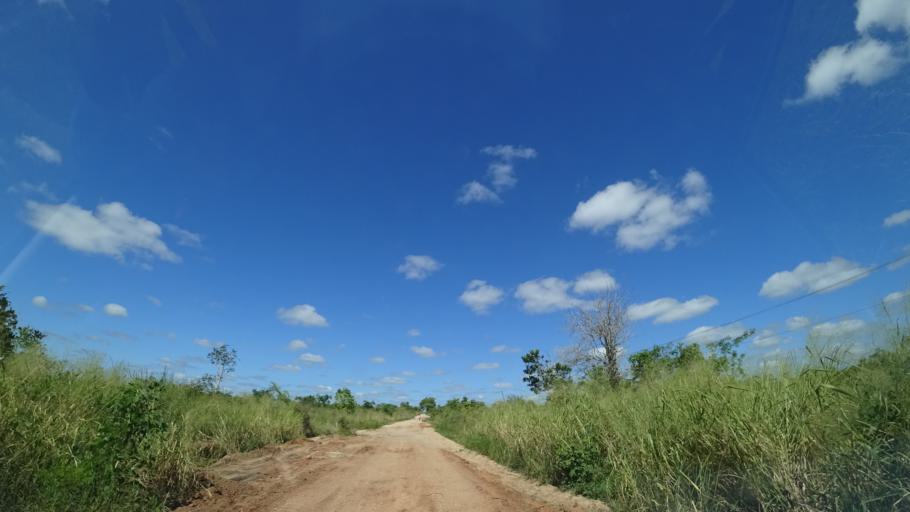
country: MZ
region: Sofala
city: Dondo
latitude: -19.3164
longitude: 34.6905
